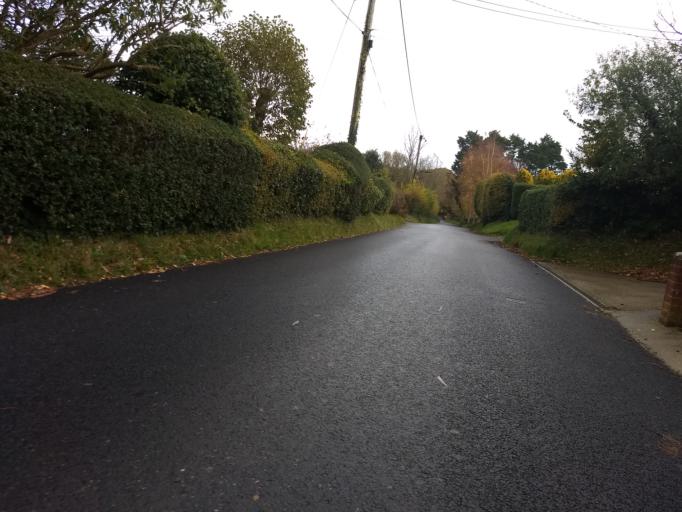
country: GB
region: England
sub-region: Isle of Wight
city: Freshwater
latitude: 50.6750
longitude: -1.5135
